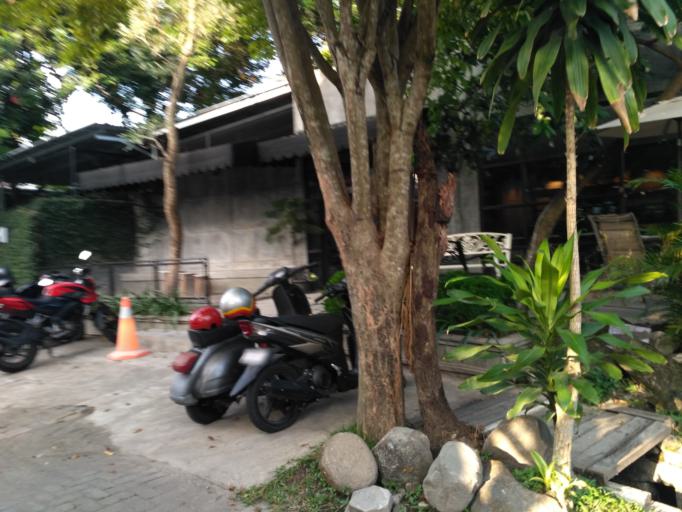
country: ID
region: Daerah Istimewa Yogyakarta
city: Yogyakarta
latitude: -7.7597
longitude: 110.3762
